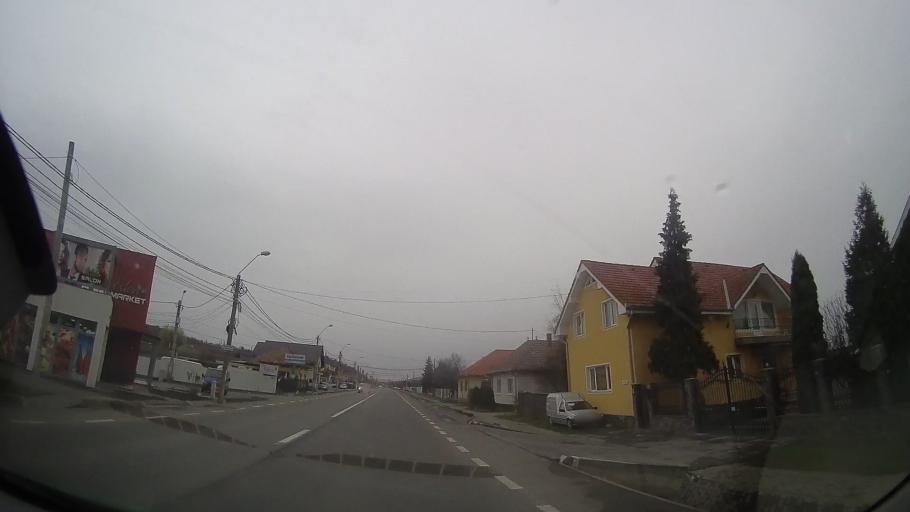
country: RO
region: Mures
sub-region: Comuna Santana de Mures
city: Santana de Mures
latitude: 46.5877
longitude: 24.5367
